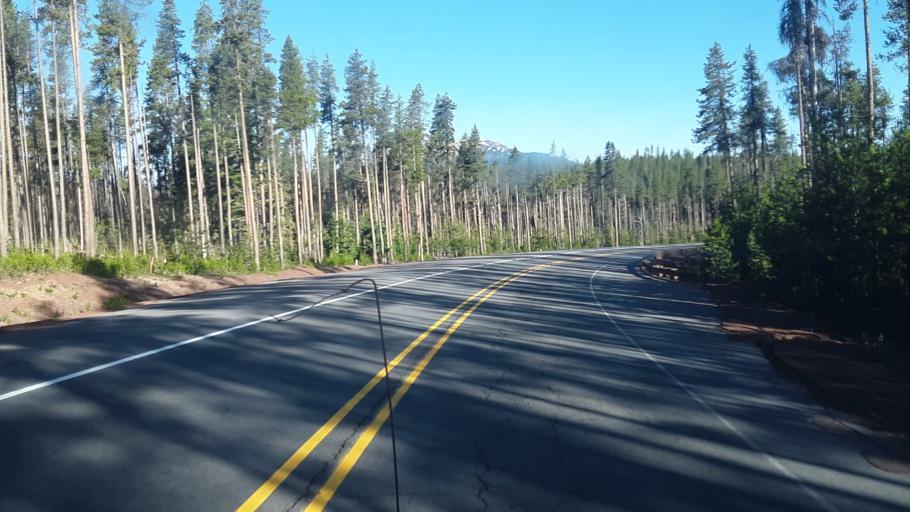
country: US
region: Oregon
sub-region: Lane County
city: Oakridge
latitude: 43.1000
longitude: -122.1290
